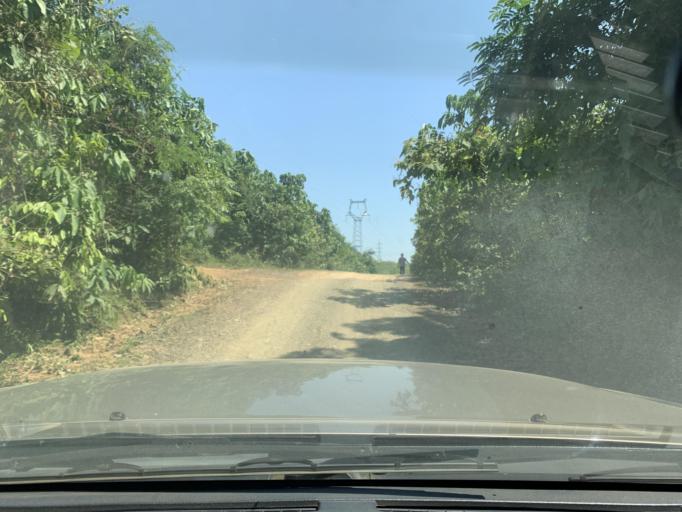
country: LA
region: Louangphabang
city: Louangphabang
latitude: 19.8992
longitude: 102.2153
